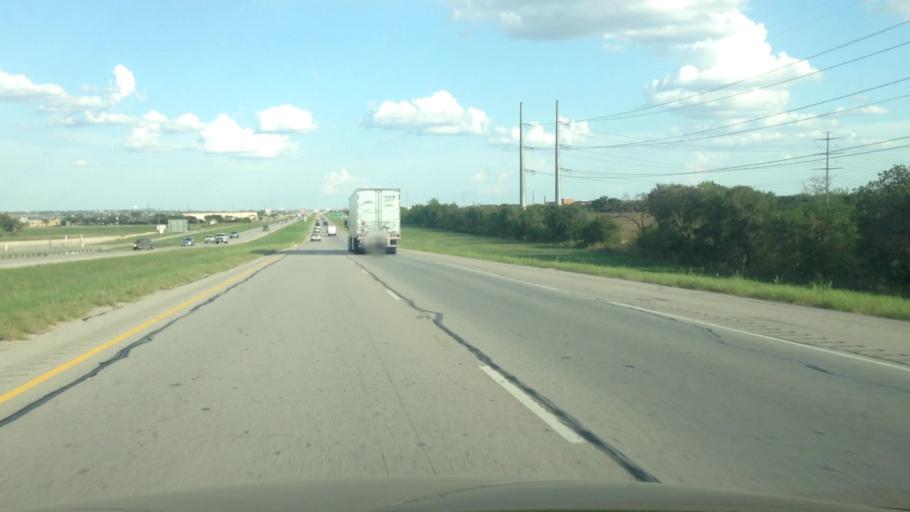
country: US
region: Texas
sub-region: Tarrant County
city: Haslet
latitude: 32.9579
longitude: -97.4052
